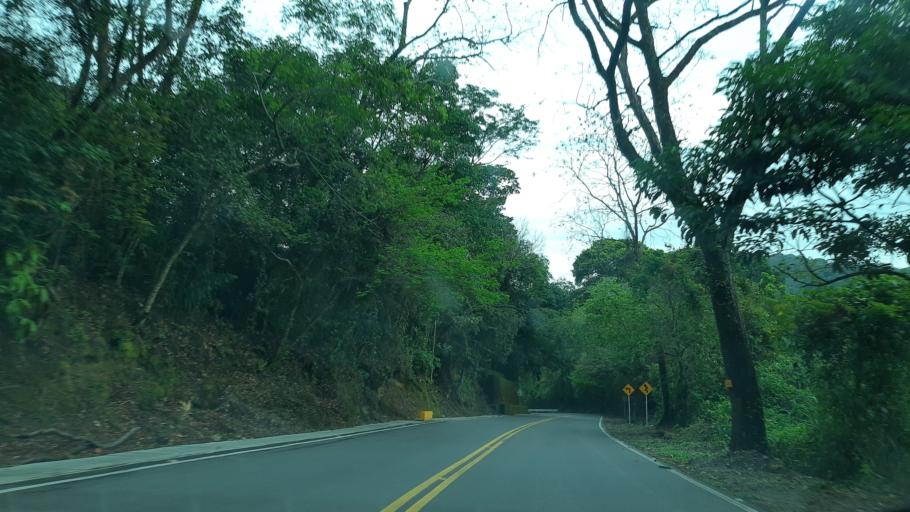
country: CO
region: Casanare
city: Sabanalarga
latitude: 4.7524
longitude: -73.0165
